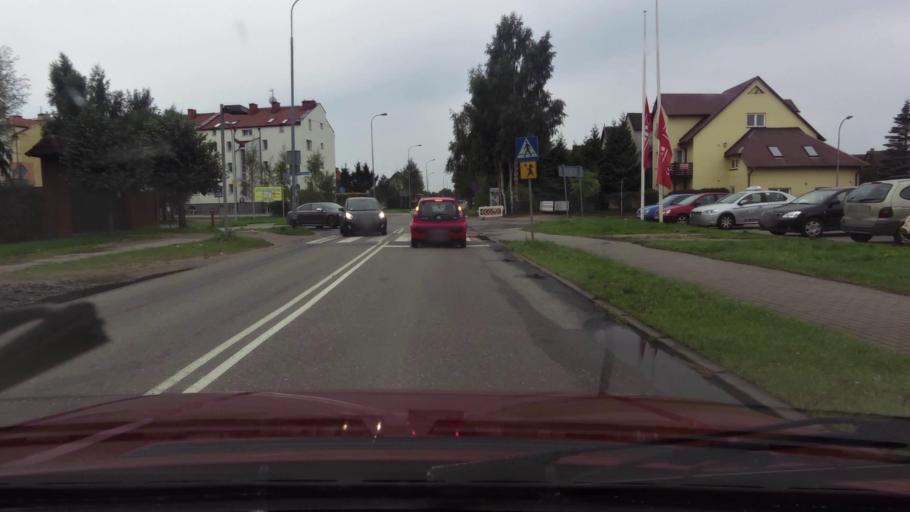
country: PL
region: West Pomeranian Voivodeship
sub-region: Powiat kolobrzeski
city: Kolobrzeg
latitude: 54.1557
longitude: 15.5436
